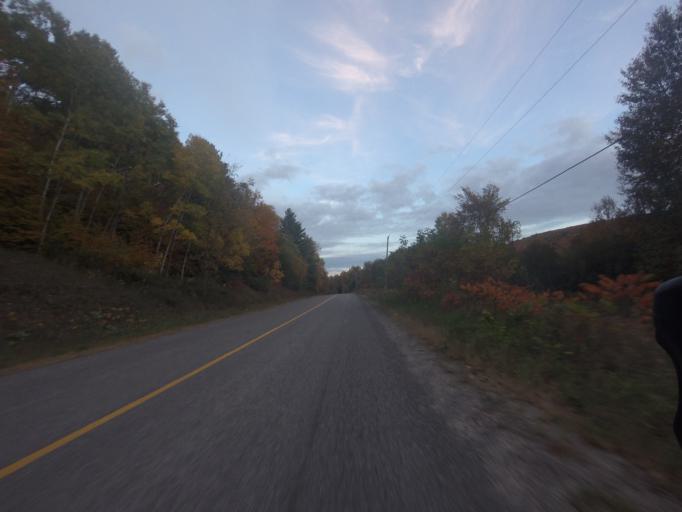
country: CA
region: Ontario
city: Renfrew
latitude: 45.3593
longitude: -76.9650
